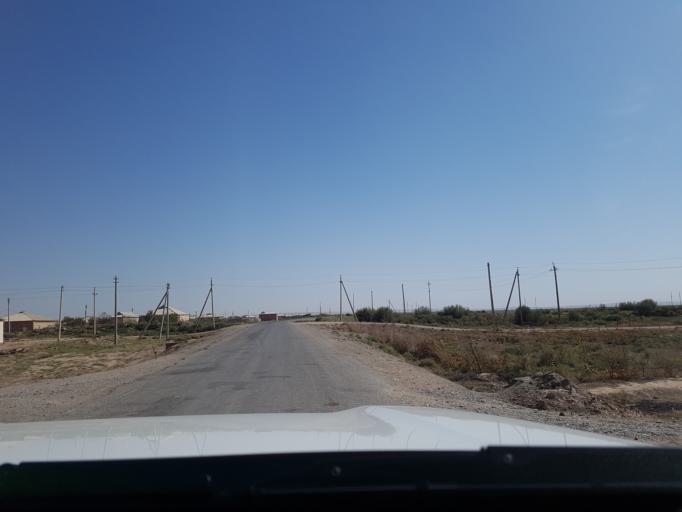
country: IR
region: Razavi Khorasan
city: Sarakhs
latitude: 36.5166
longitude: 61.2519
